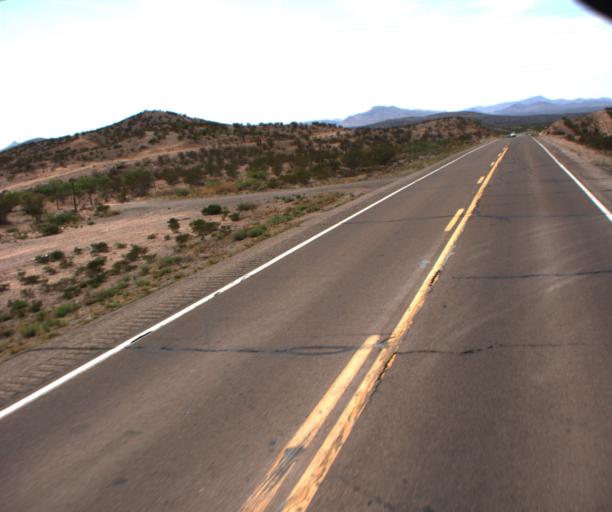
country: US
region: Arizona
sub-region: Greenlee County
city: Clifton
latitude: 32.7625
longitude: -109.1419
